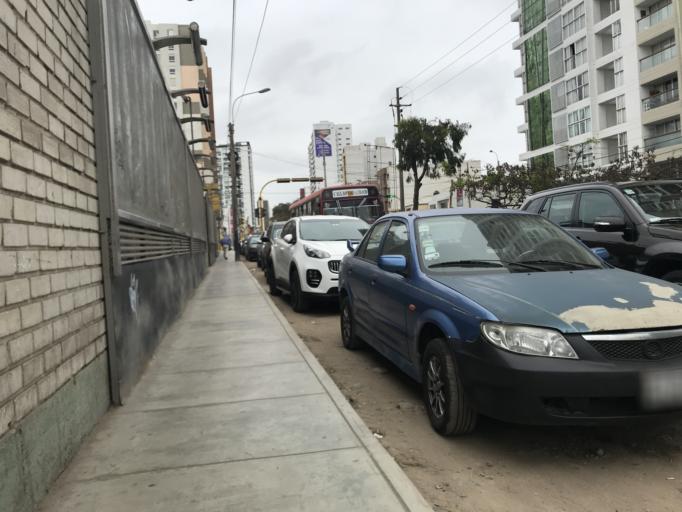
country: PE
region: Callao
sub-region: Callao
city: Callao
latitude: -12.0755
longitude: -77.0768
